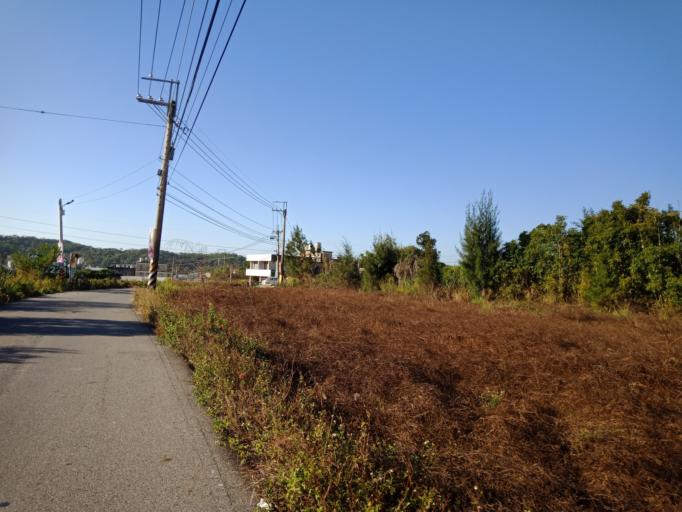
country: TW
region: Taiwan
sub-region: Miaoli
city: Miaoli
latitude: 24.4921
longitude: 120.6953
